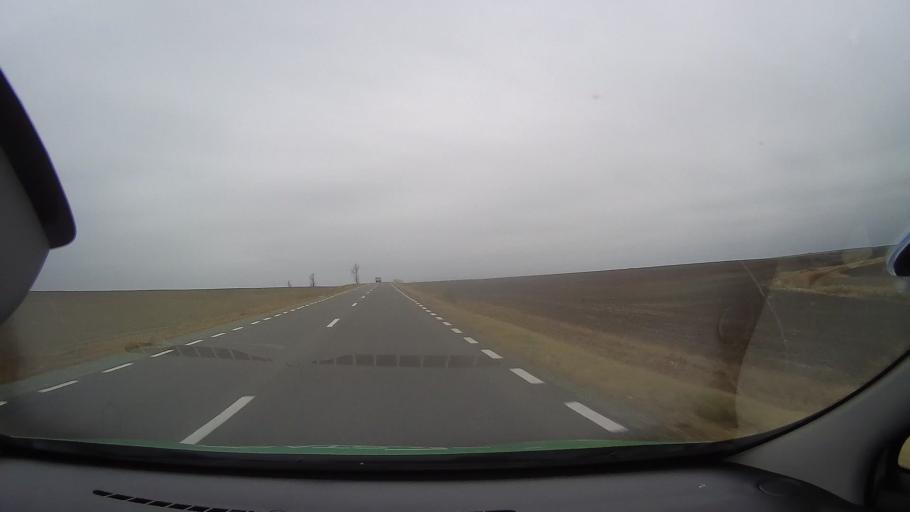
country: RO
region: Ialomita
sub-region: Comuna Scanteia
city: Iazu
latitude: 44.7185
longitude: 27.4208
